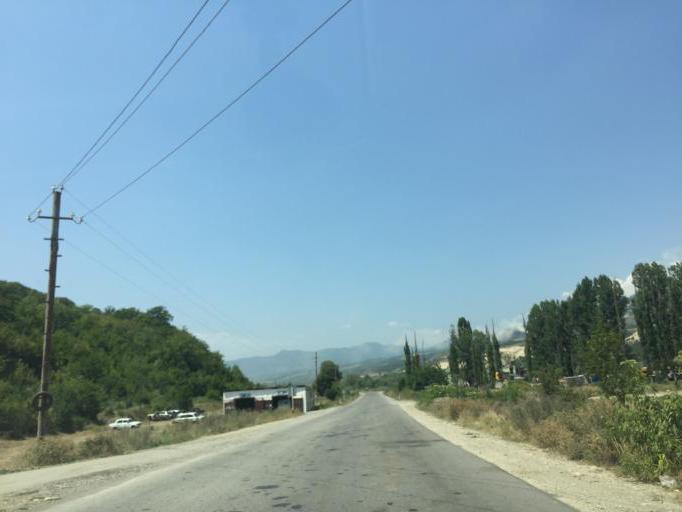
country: AZ
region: Tartar Rayon
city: Martakert
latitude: 40.1393
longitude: 46.5477
